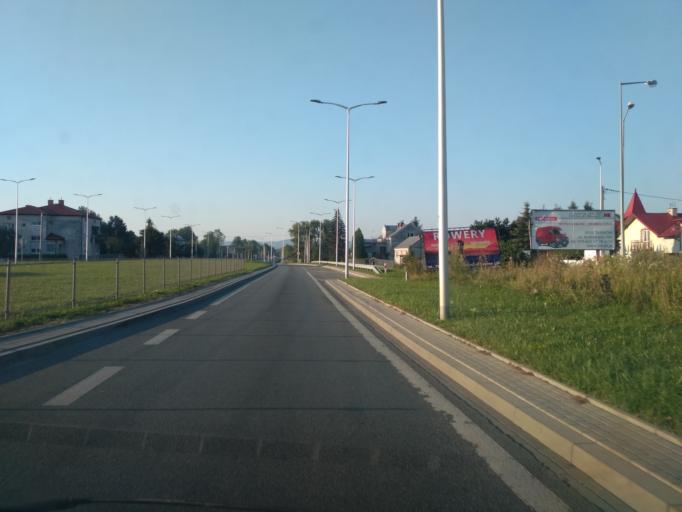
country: PL
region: Subcarpathian Voivodeship
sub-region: Krosno
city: Krosno
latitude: 49.6739
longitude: 21.7746
